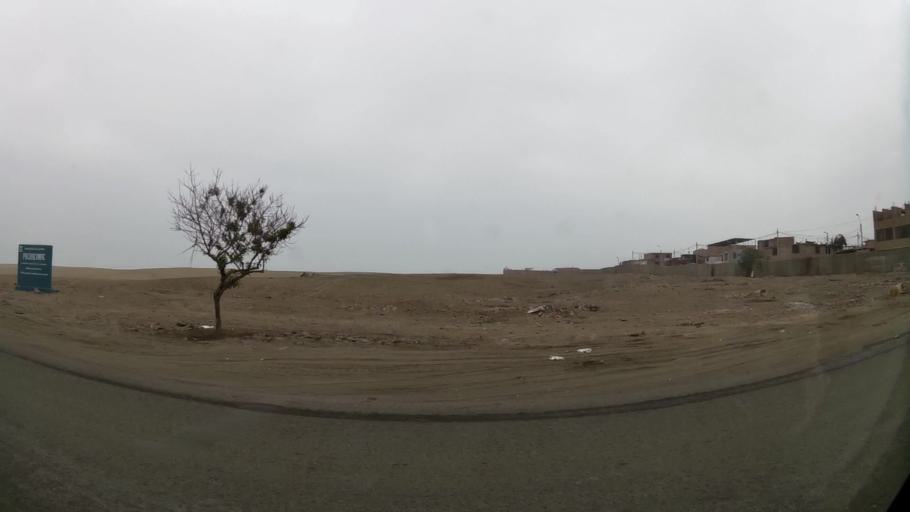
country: PE
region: Lima
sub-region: Lima
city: Punta Hermosa
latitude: -12.2413
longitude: -76.9113
